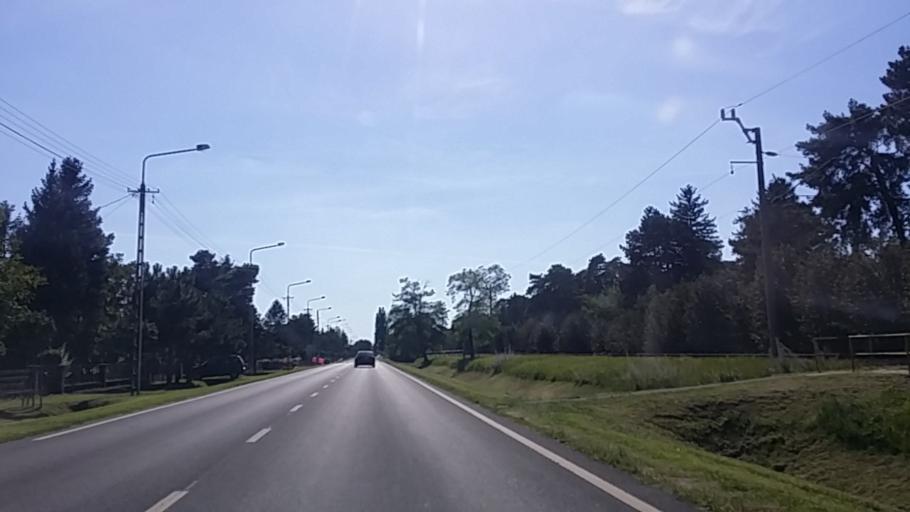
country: HU
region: Somogy
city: Balatonfenyves
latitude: 46.7185
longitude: 17.5025
